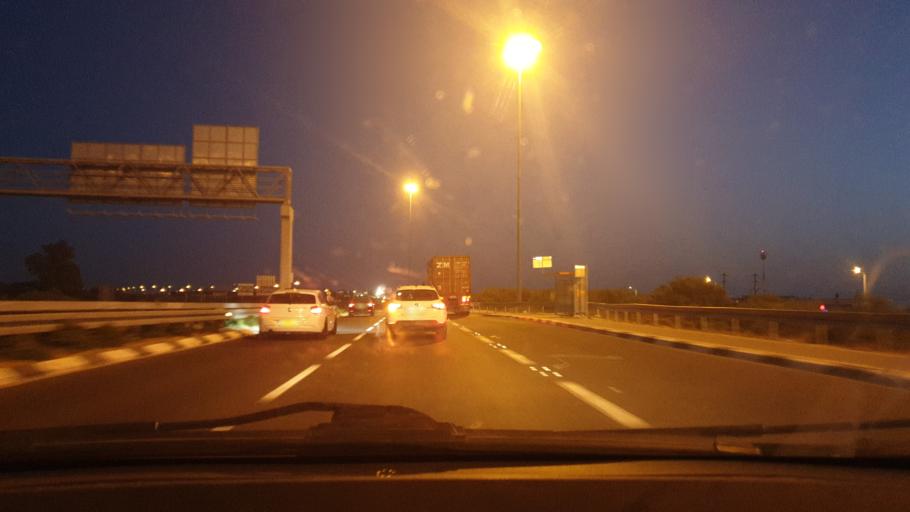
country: IL
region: Central District
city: Gedera
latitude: 31.8030
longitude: 34.7642
